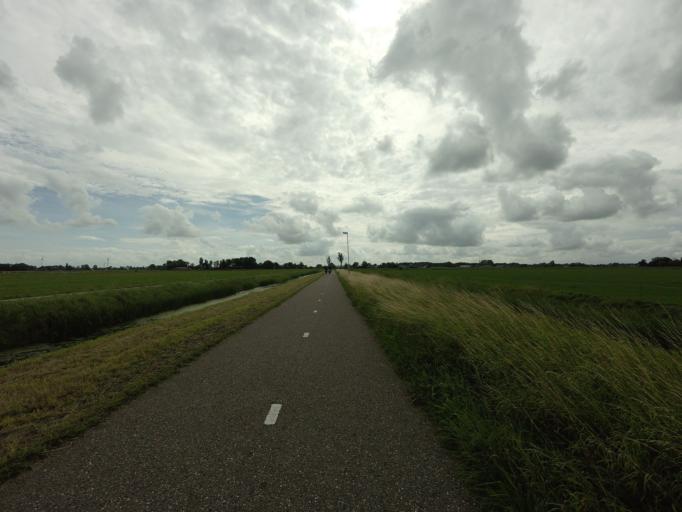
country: NL
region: North Holland
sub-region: Gemeente Medemblik
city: Opperdoes
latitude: 52.7048
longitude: 5.0697
